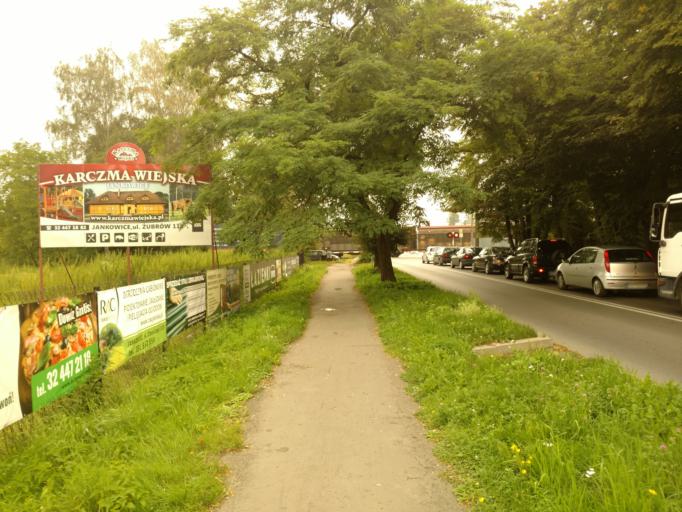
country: PL
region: Silesian Voivodeship
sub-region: Powiat pszczynski
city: Pszczyna
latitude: 49.9887
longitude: 18.9522
